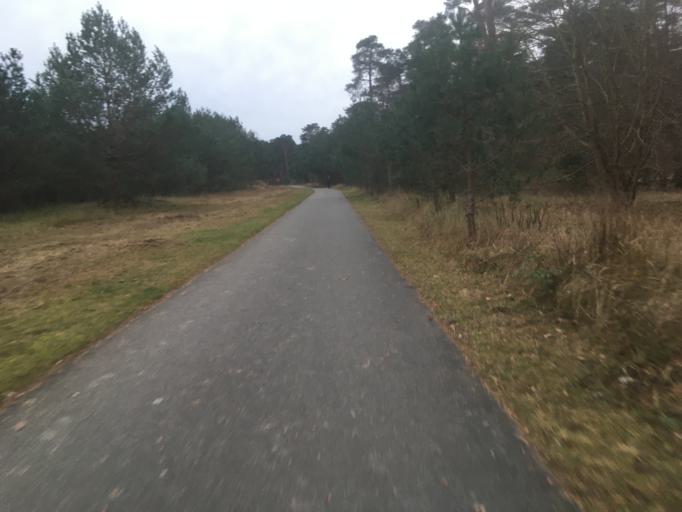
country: DE
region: Mecklenburg-Vorpommern
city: Sagard
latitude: 54.4735
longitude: 13.5685
